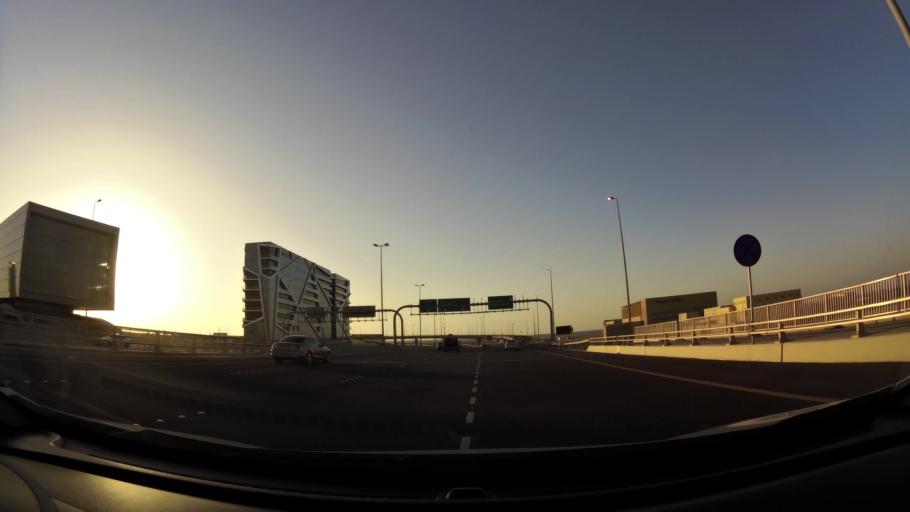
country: BH
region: Muharraq
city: Al Muharraq
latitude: 26.2507
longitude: 50.5852
